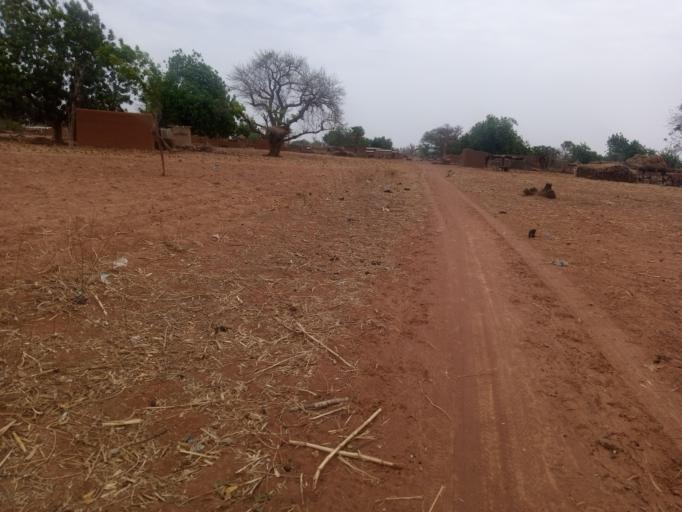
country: BF
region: Boucle du Mouhoun
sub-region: Province de la Kossi
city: Nouna
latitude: 12.8540
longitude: -4.0756
